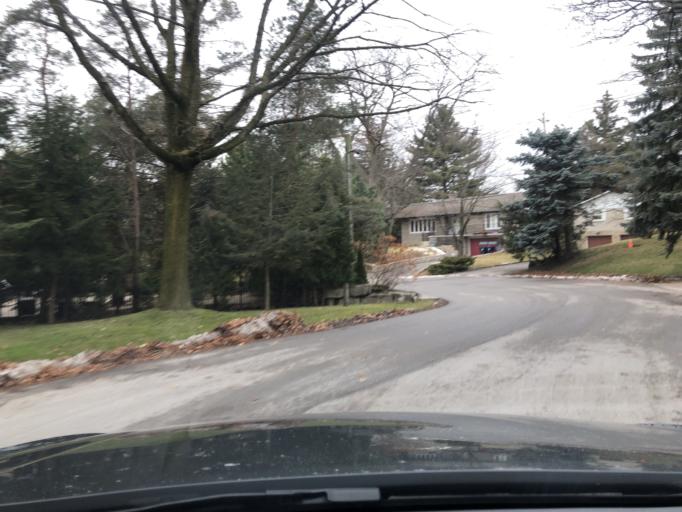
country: CA
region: Ontario
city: Etobicoke
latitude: 43.6939
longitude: -79.5244
